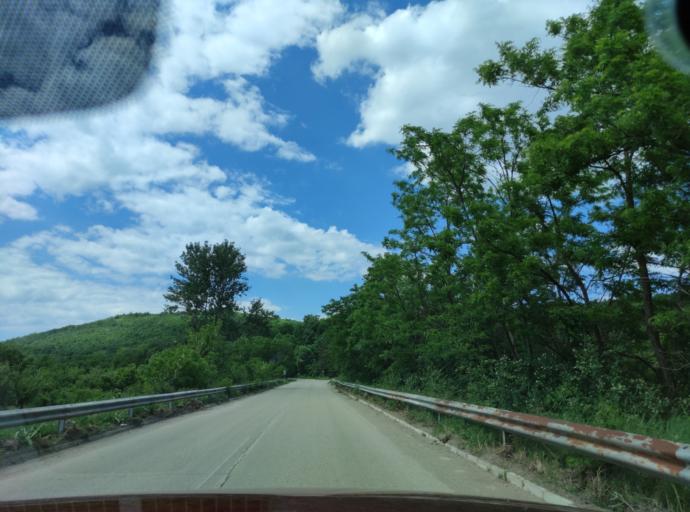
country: BG
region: Montana
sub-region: Obshtina Montana
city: Montana
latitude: 43.4032
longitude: 23.0693
